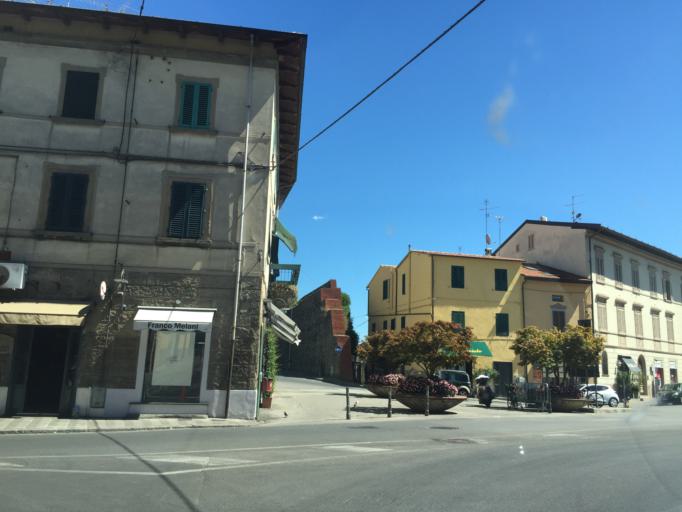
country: IT
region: Tuscany
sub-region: Provincia di Pistoia
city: Pistoia
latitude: 43.9288
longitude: 10.9181
